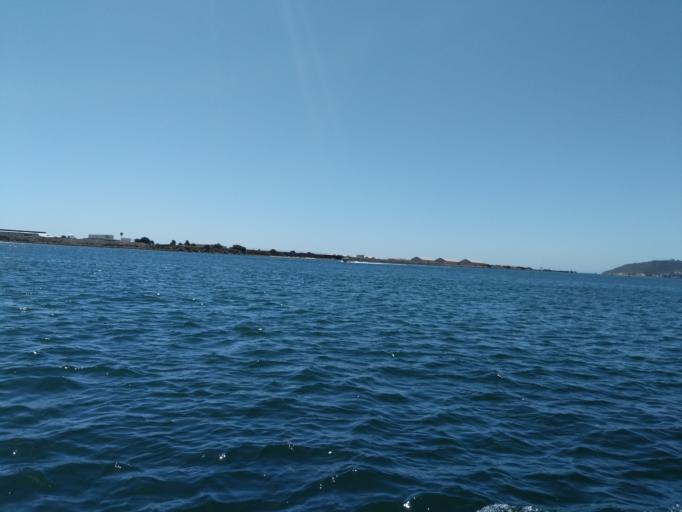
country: US
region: California
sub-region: San Diego County
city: Coronado
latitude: 32.7114
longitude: -117.2243
